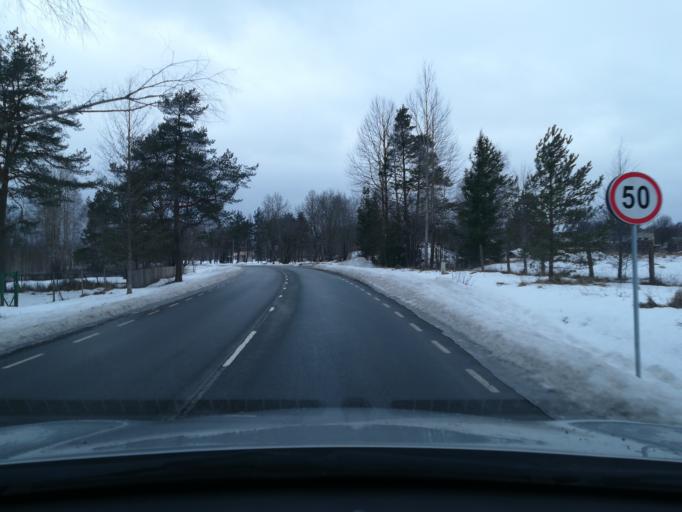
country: EE
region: Harju
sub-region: Nissi vald
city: Turba
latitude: 59.0720
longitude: 24.2486
